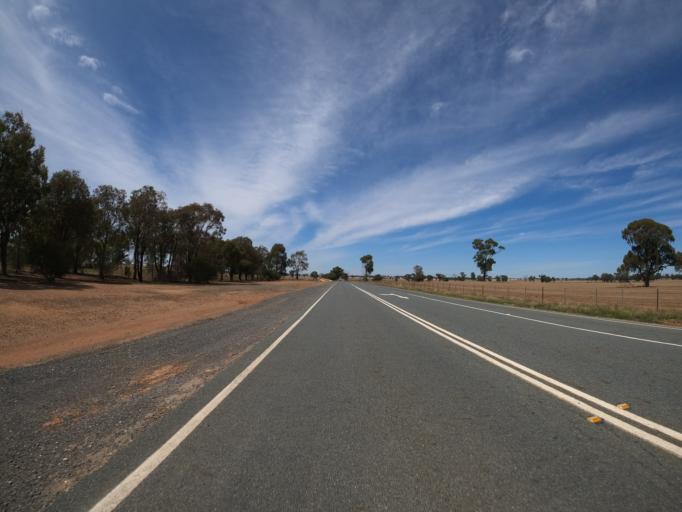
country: AU
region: Victoria
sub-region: Moira
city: Yarrawonga
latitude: -36.0489
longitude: 145.9955
